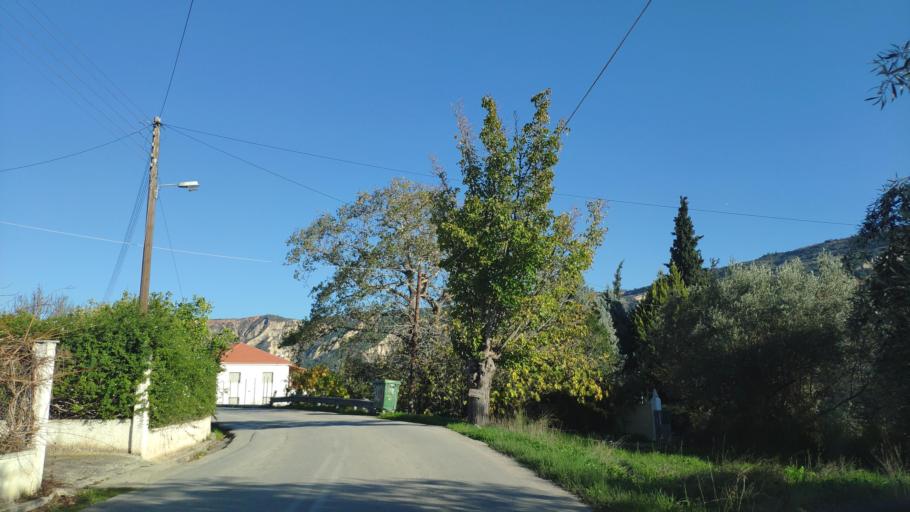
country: GR
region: Peloponnese
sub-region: Nomos Korinthias
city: Xylokastro
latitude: 38.0536
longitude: 22.5968
